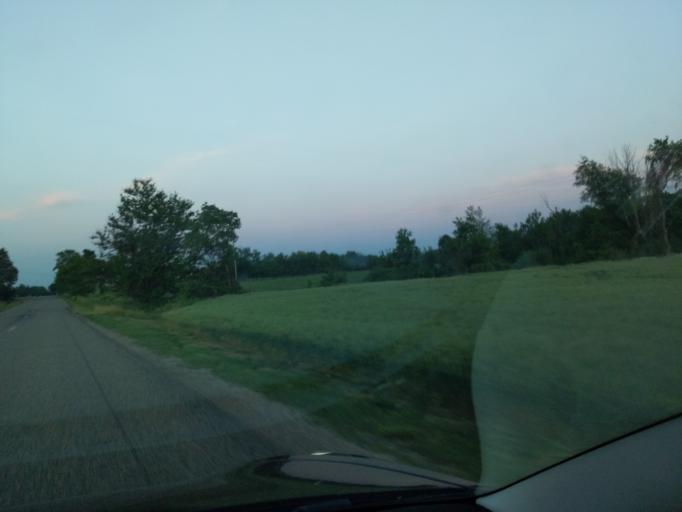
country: US
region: Michigan
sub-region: Eaton County
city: Bellevue
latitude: 42.5385
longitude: -84.9899
